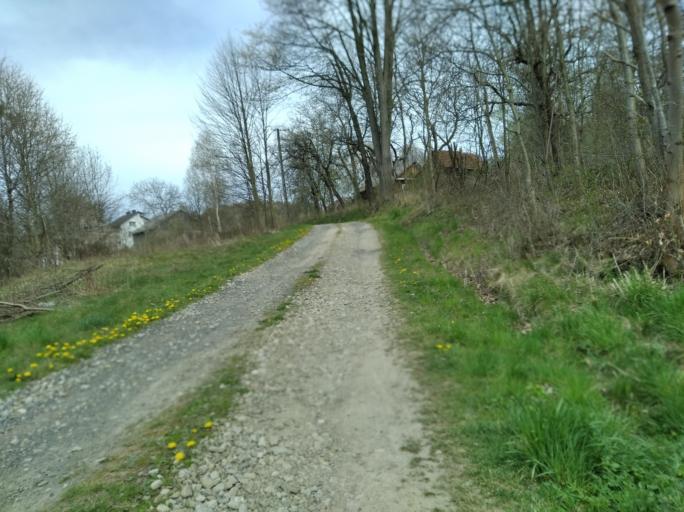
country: PL
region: Subcarpathian Voivodeship
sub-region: Powiat ropczycko-sedziszowski
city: Wielopole Skrzynskie
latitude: 49.9085
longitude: 21.6143
